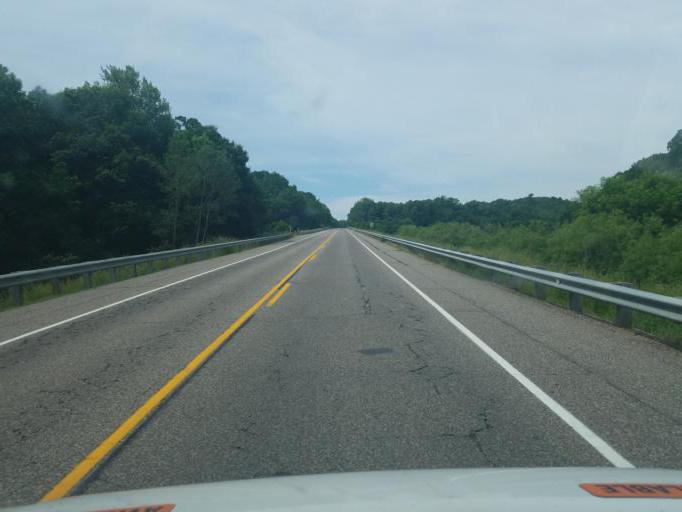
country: US
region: Wisconsin
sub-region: Juneau County
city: New Lisbon
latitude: 43.7862
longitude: -90.1875
